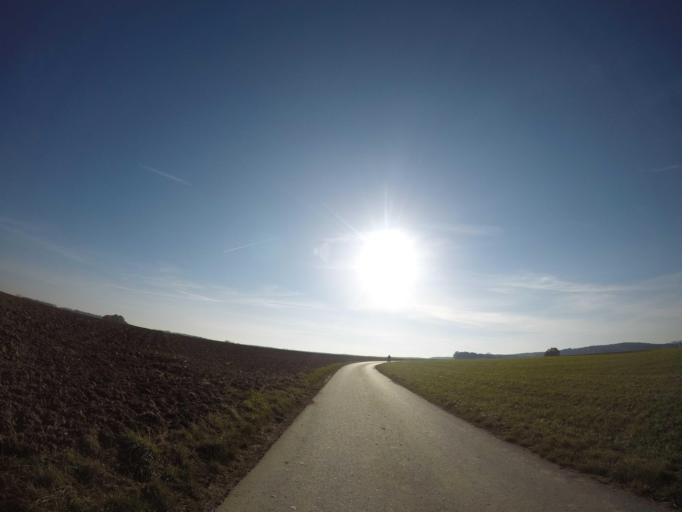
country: DE
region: Baden-Wuerttemberg
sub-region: Tuebingen Region
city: Emerkingen
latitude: 48.2030
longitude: 9.6545
